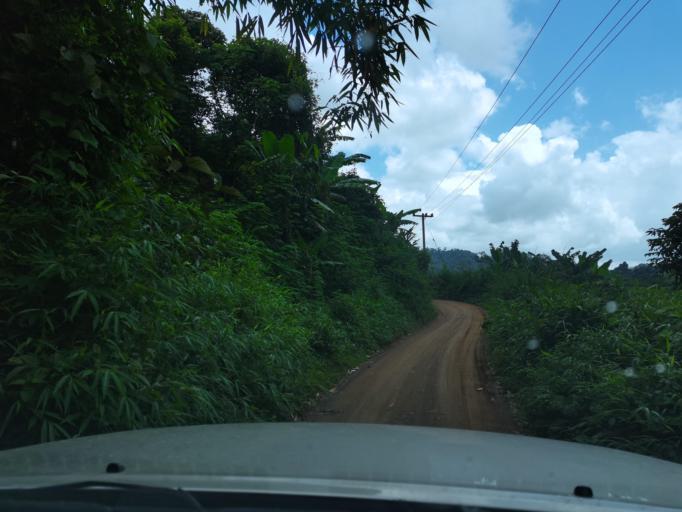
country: LA
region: Loungnamtha
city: Muang Long
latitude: 20.7555
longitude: 101.0173
